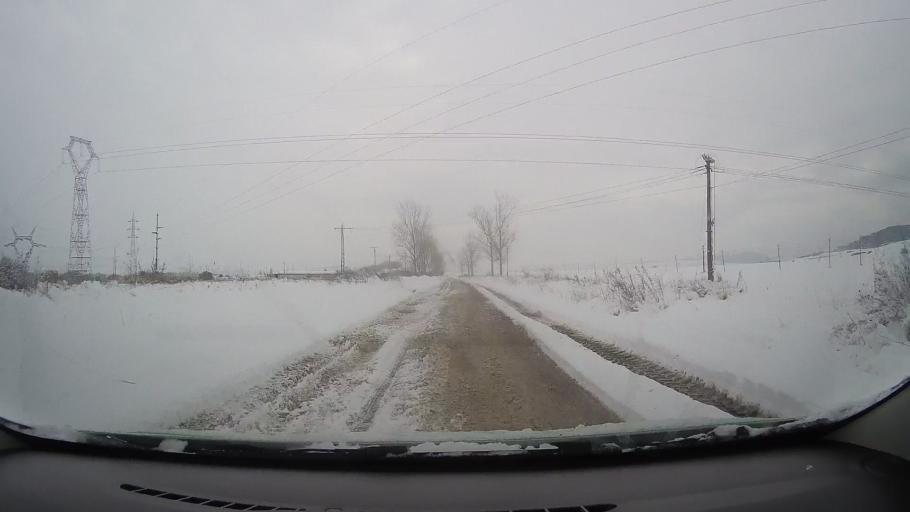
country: RO
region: Alba
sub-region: Comuna Pianu
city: Pianu de Jos
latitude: 45.9617
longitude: 23.5082
